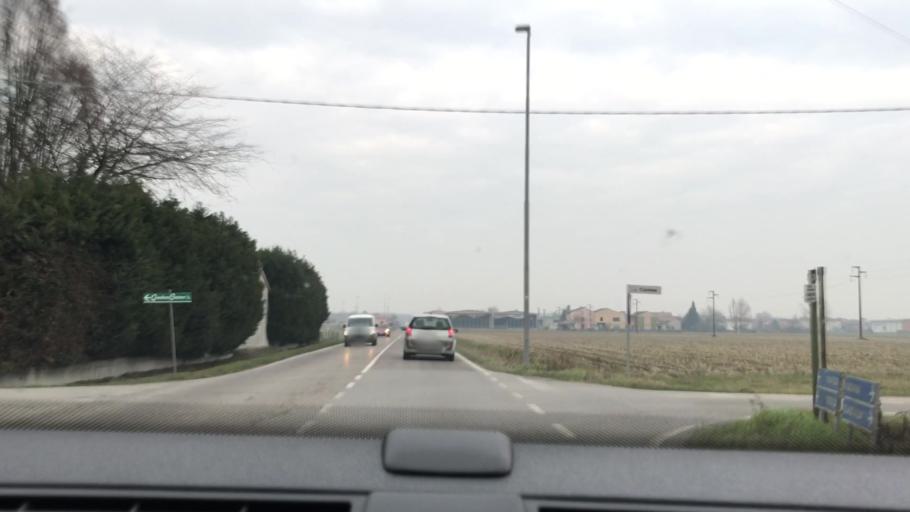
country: IT
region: Lombardy
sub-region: Provincia di Mantova
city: Dosolo
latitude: 44.9457
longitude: 10.6281
